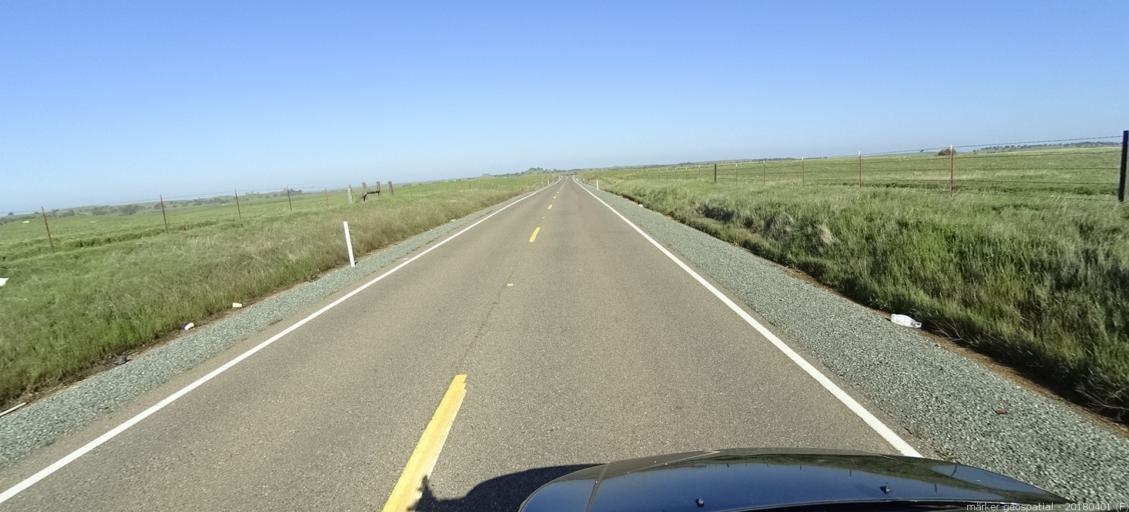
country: US
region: California
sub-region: Sacramento County
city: Rancho Murieta
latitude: 38.4104
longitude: -121.0317
